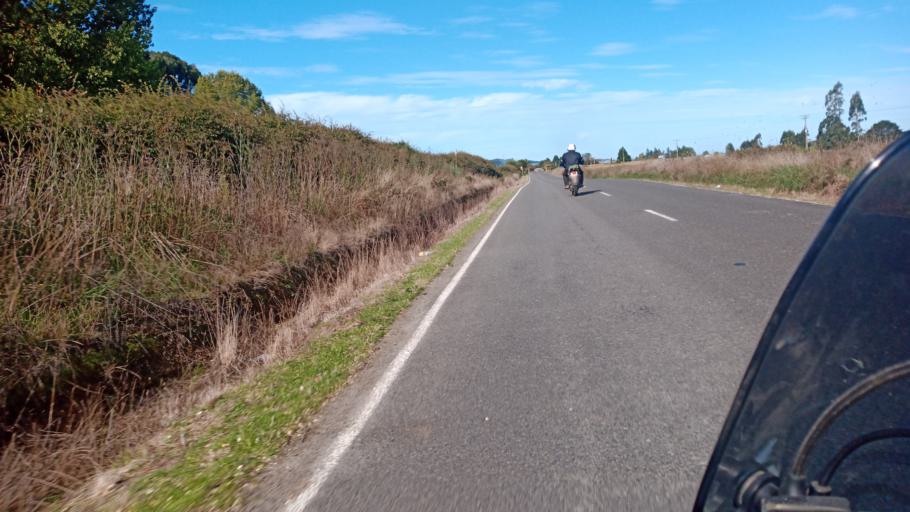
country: NZ
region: Hawke's Bay
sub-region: Wairoa District
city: Wairoa
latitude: -39.0678
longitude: 177.1386
